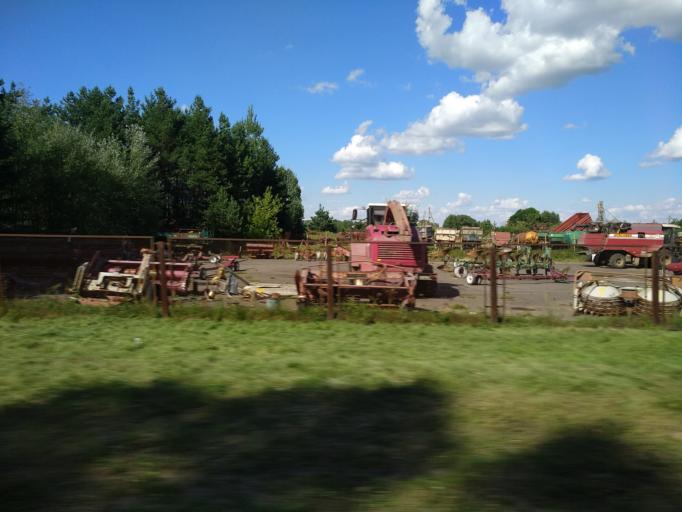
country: BY
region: Vitebsk
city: Mosar
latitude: 55.0748
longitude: 27.2221
